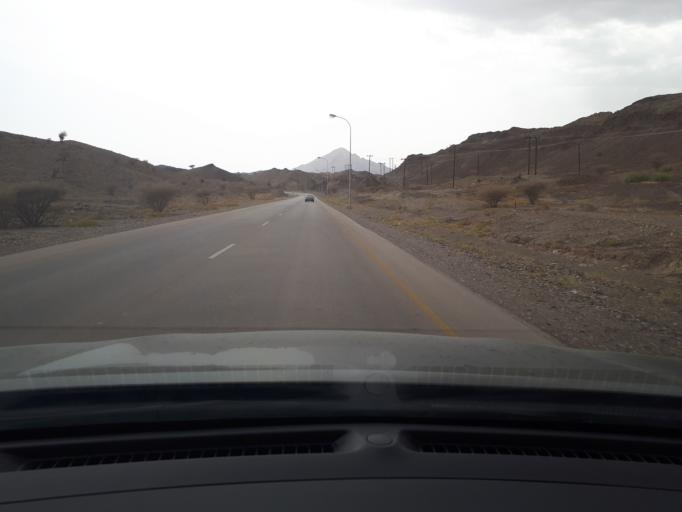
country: OM
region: Ash Sharqiyah
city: Badiyah
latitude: 22.5563
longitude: 59.0120
